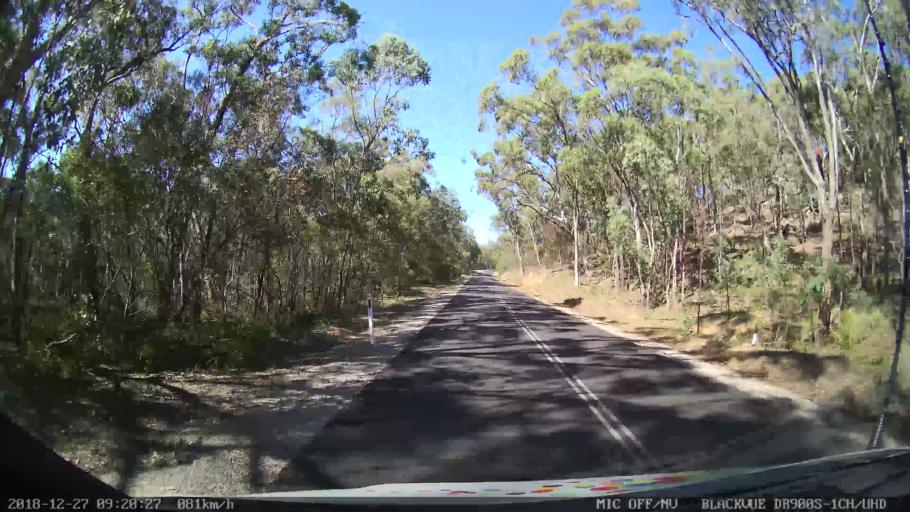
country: AU
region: New South Wales
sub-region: Lithgow
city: Portland
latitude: -33.1195
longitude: 150.0226
